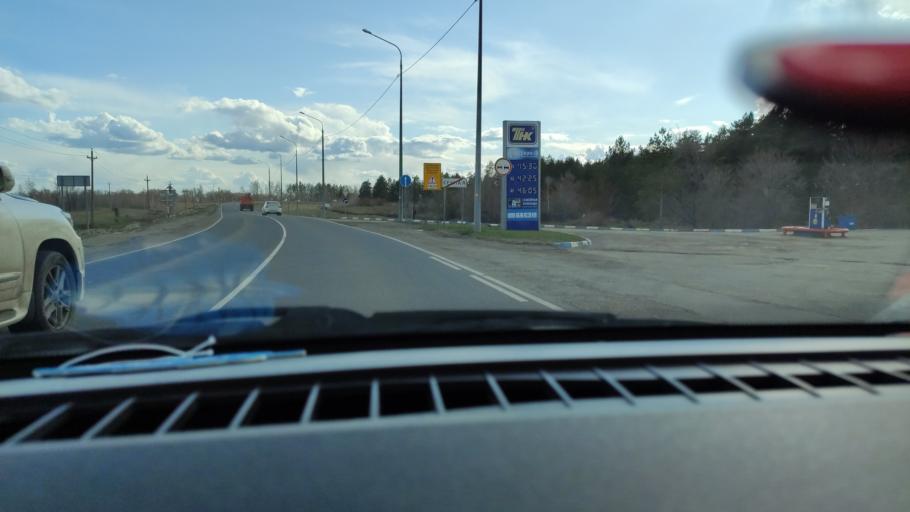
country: RU
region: Saratov
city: Sennoy
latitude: 52.1474
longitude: 46.9462
